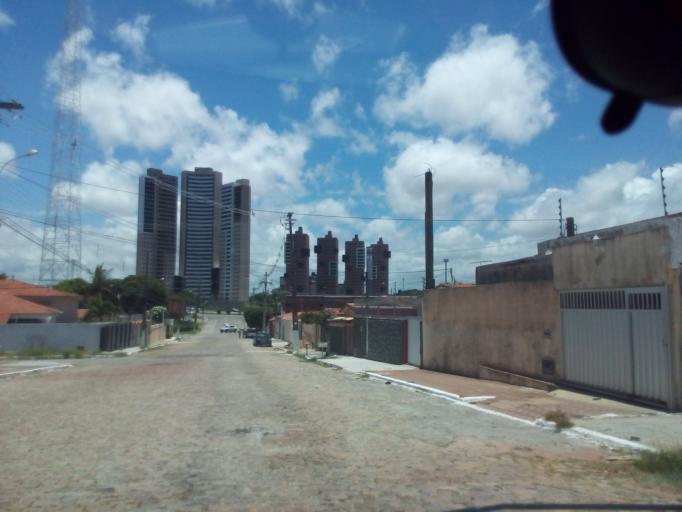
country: BR
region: Rio Grande do Norte
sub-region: Natal
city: Natal
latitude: -5.8454
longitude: -35.2069
